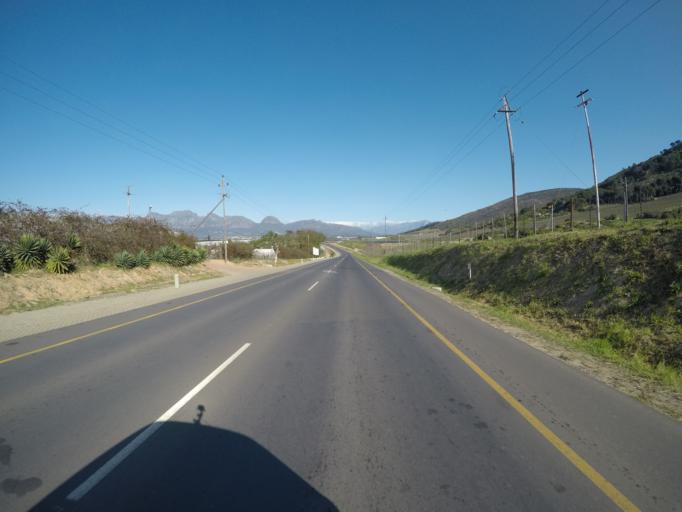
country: ZA
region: Western Cape
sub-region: Cape Winelands District Municipality
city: Noorder-Paarl
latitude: -33.6849
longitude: 18.9479
